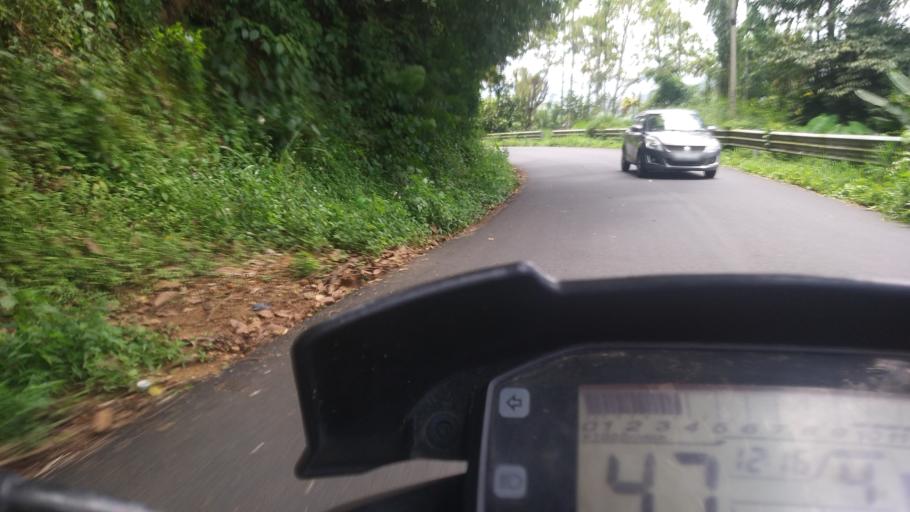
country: IN
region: Kerala
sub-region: Idukki
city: Munnar
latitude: 10.0152
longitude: 77.0114
